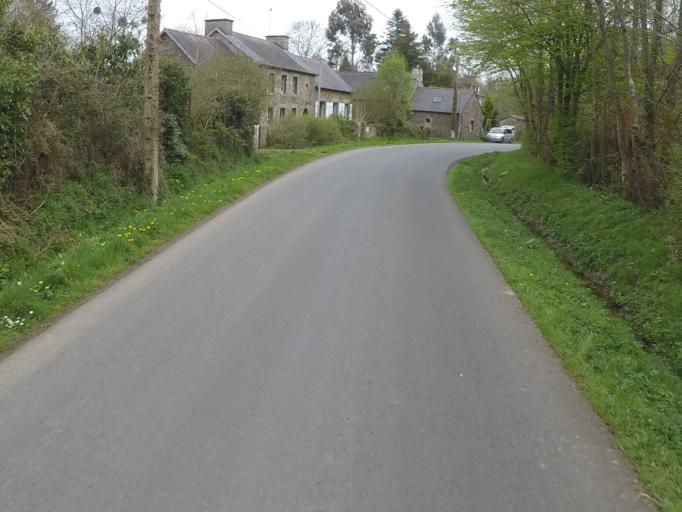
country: FR
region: Brittany
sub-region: Departement des Cotes-d'Armor
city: Plouha
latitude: 48.6624
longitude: -2.9182
